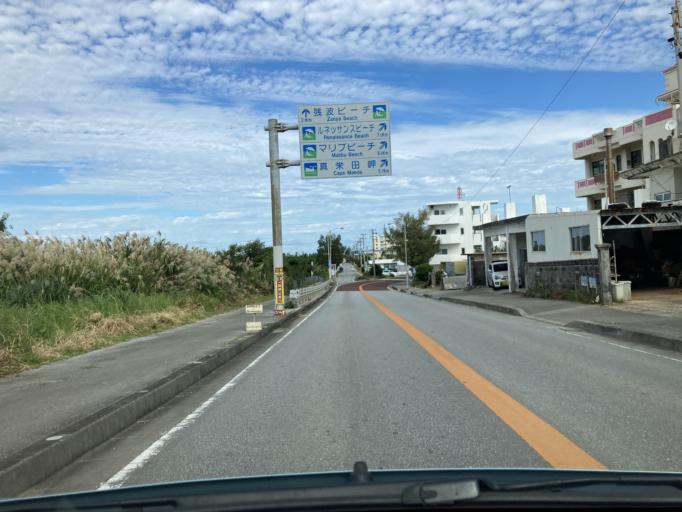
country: JP
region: Okinawa
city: Ishikawa
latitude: 26.4231
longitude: 127.7306
